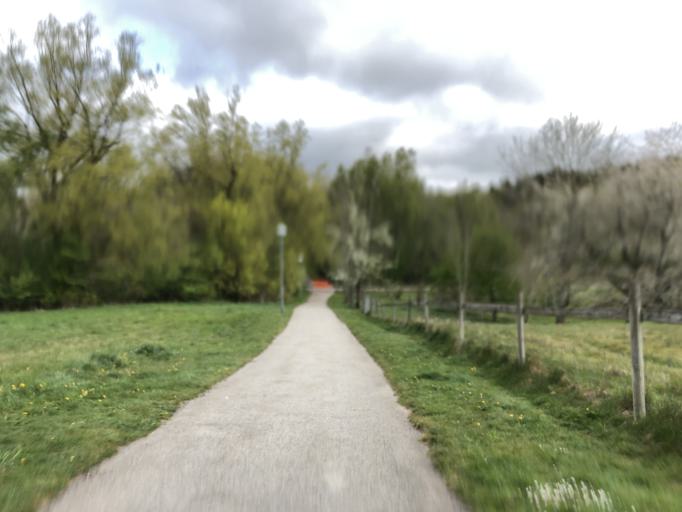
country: SE
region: Skane
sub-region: Lunds Kommun
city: Genarp
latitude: 55.6718
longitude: 13.3551
